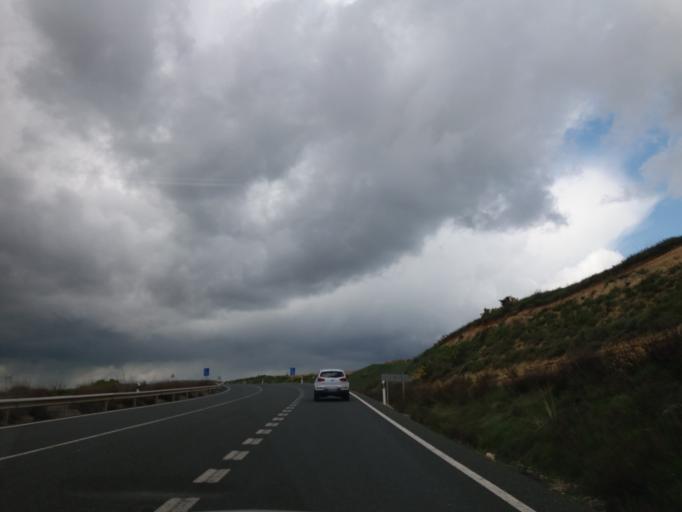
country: ES
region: La Rioja
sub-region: Provincia de La Rioja
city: Ollauri
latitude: 42.5441
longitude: -2.8504
